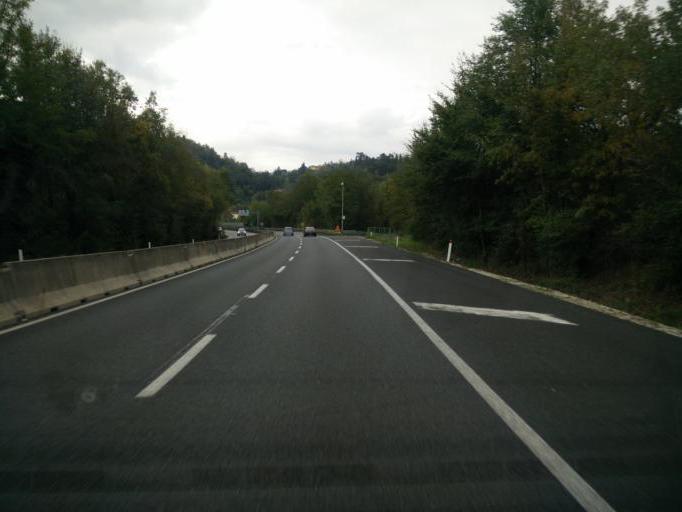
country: IT
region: Tuscany
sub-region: Province of Florence
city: Tavarnuzze
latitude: 43.6993
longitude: 11.2128
